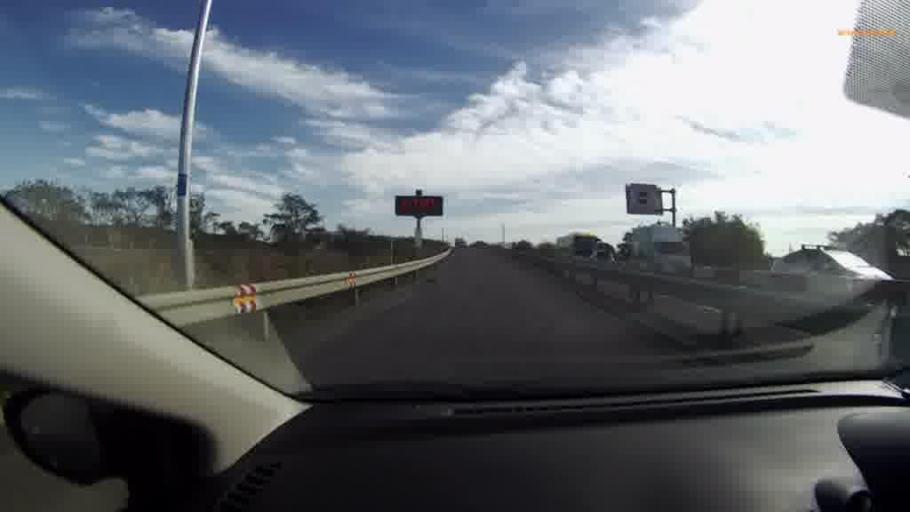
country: JP
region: Hokkaido
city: Kushiro
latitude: 43.0365
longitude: 144.3267
